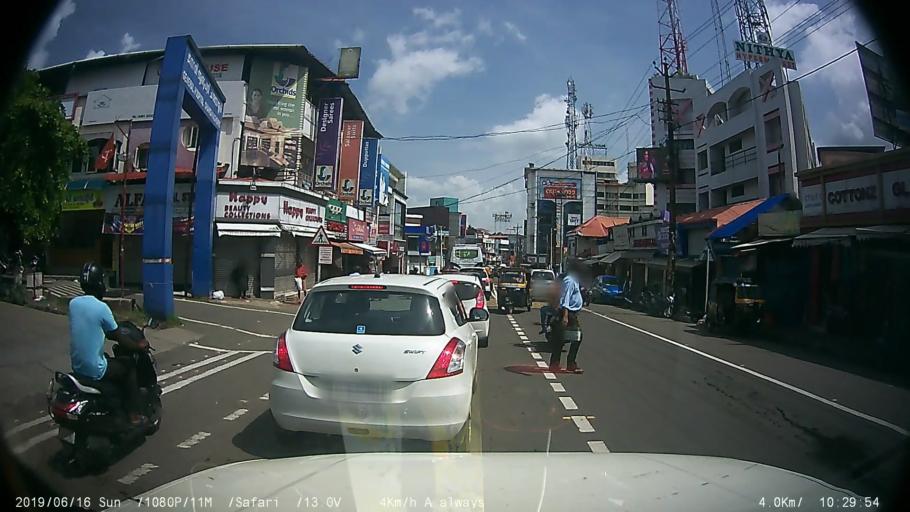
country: IN
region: Kerala
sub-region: Kottayam
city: Changanacheri
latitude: 9.4459
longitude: 76.5410
